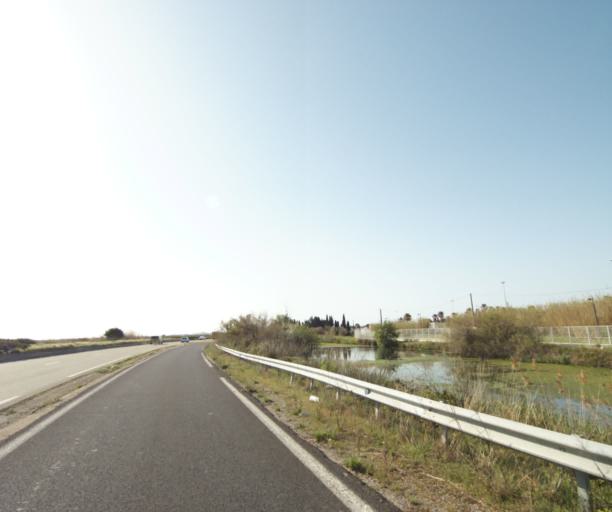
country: FR
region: Languedoc-Roussillon
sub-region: Departement de l'Herault
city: Perols
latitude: 43.5725
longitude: 3.9544
